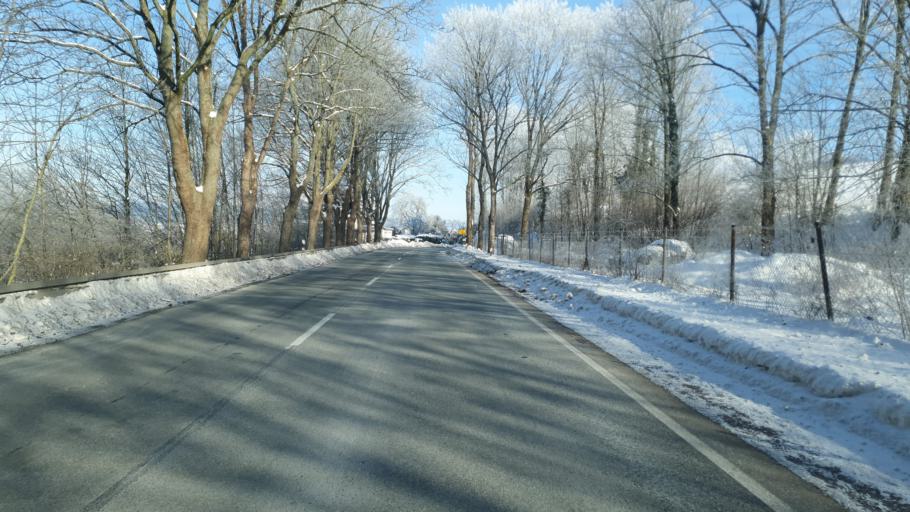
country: DE
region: Lower Saxony
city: Aerzen
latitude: 52.0237
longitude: 9.2251
